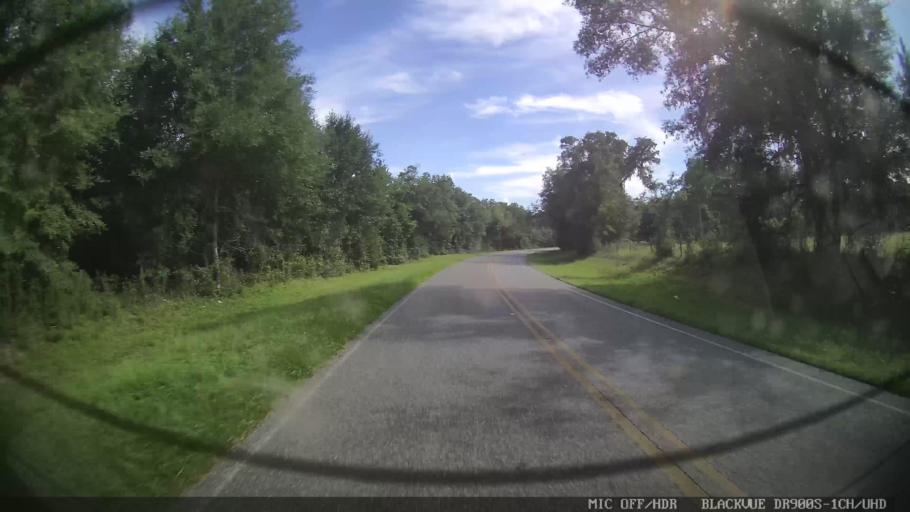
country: US
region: Georgia
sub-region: Echols County
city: Statenville
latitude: 30.6111
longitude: -83.2179
